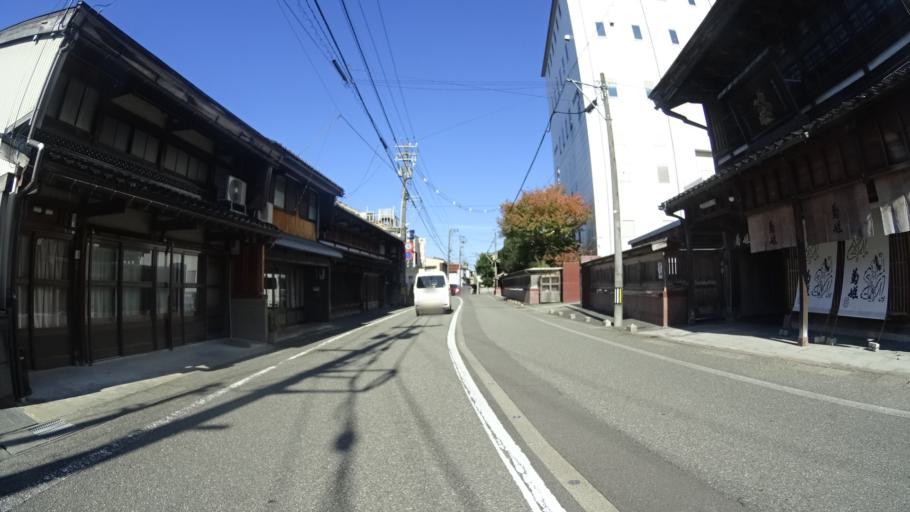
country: JP
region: Ishikawa
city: Tsurugi-asahimachi
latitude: 36.4460
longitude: 136.6289
